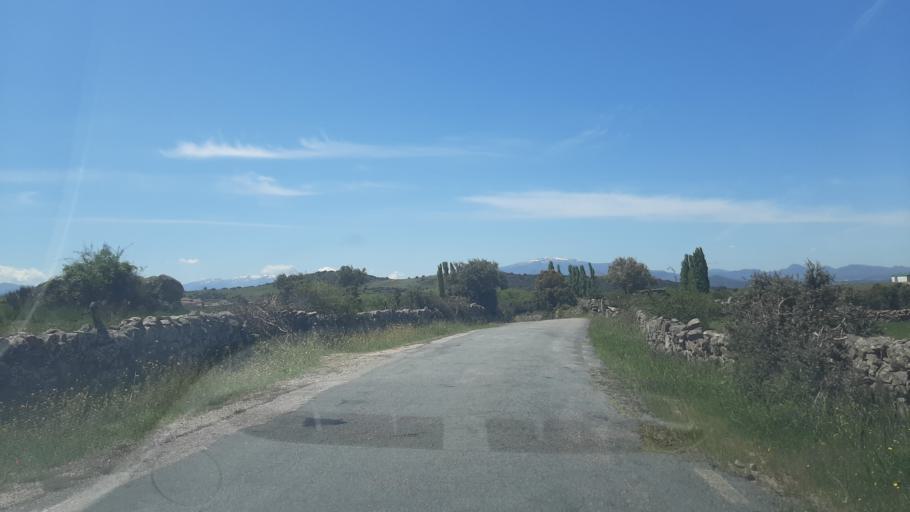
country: ES
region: Castille and Leon
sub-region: Provincia de Avila
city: Narrillos del Alamo
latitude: 40.5466
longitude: -5.4464
